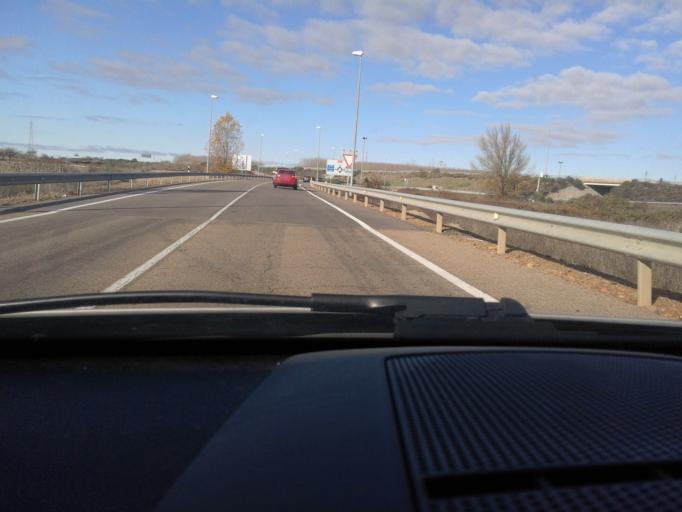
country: ES
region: Castille and Leon
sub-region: Provincia de Palencia
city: Carrion de los Condes
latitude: 42.3480
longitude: -4.6210
